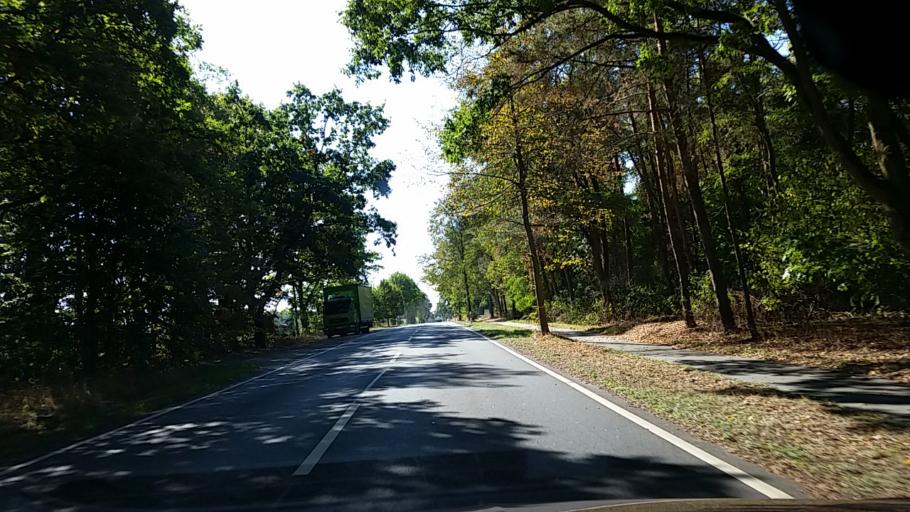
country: DE
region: Lower Saxony
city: Ruhen
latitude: 52.4636
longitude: 10.8616
